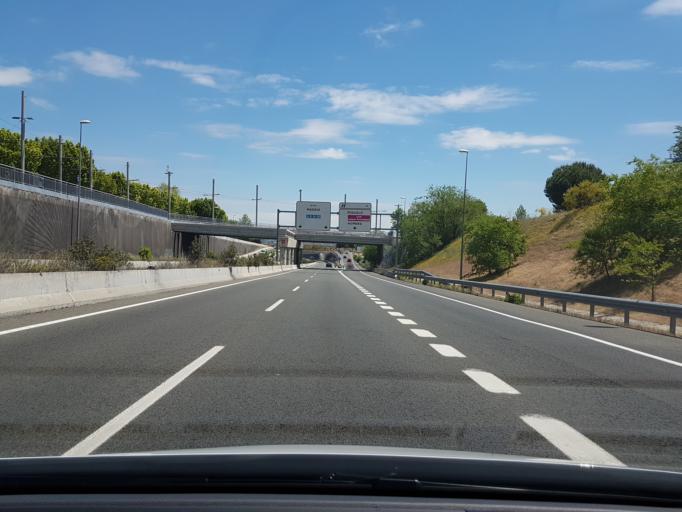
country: ES
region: Madrid
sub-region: Provincia de Madrid
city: Pozuelo de Alarcon
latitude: 40.4324
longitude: -3.8014
